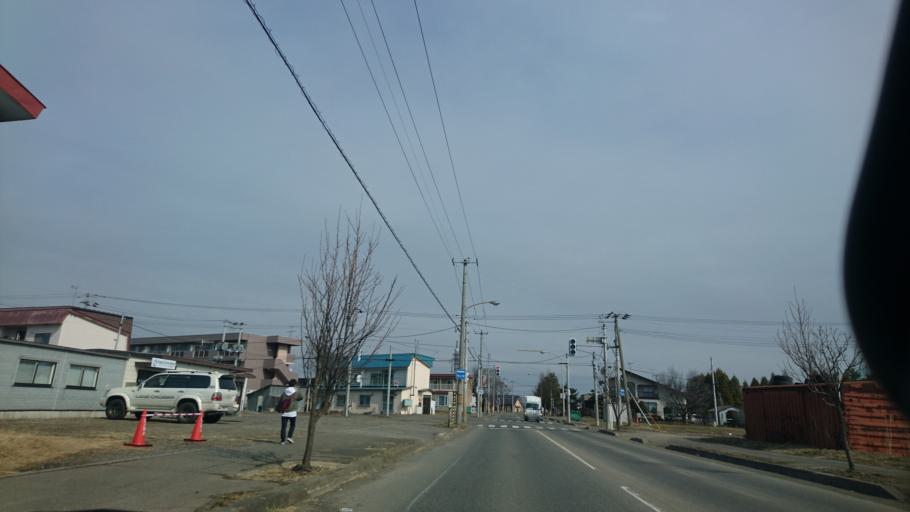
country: JP
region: Hokkaido
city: Obihiro
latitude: 42.9519
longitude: 143.2078
